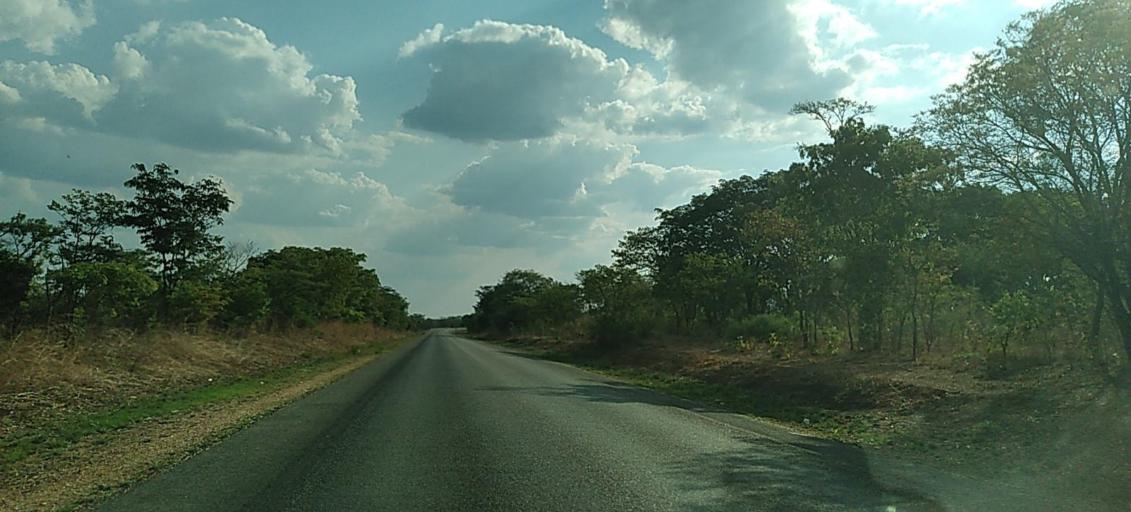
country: ZM
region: Copperbelt
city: Luanshya
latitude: -13.3833
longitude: 28.3912
